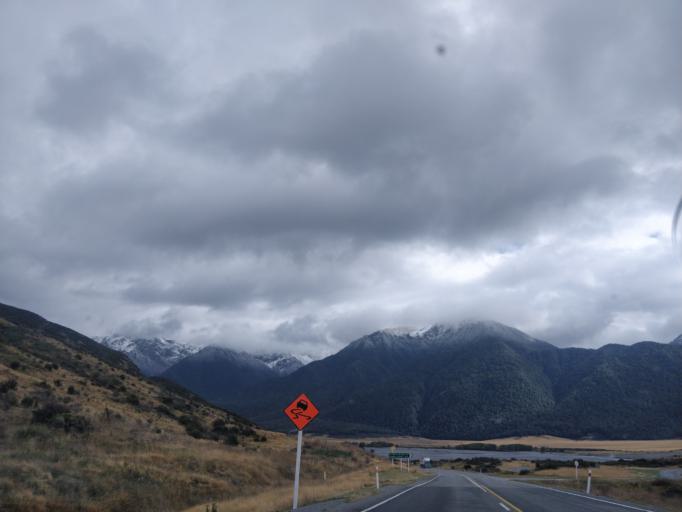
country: NZ
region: Canterbury
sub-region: Waimakariri District
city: Oxford
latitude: -43.0129
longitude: 171.7430
